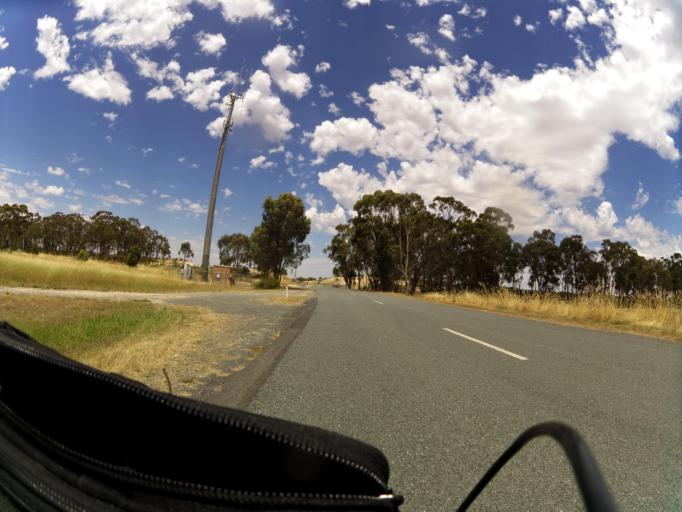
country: AU
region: Victoria
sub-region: Greater Shepparton
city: Shepparton
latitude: -36.6289
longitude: 145.2110
